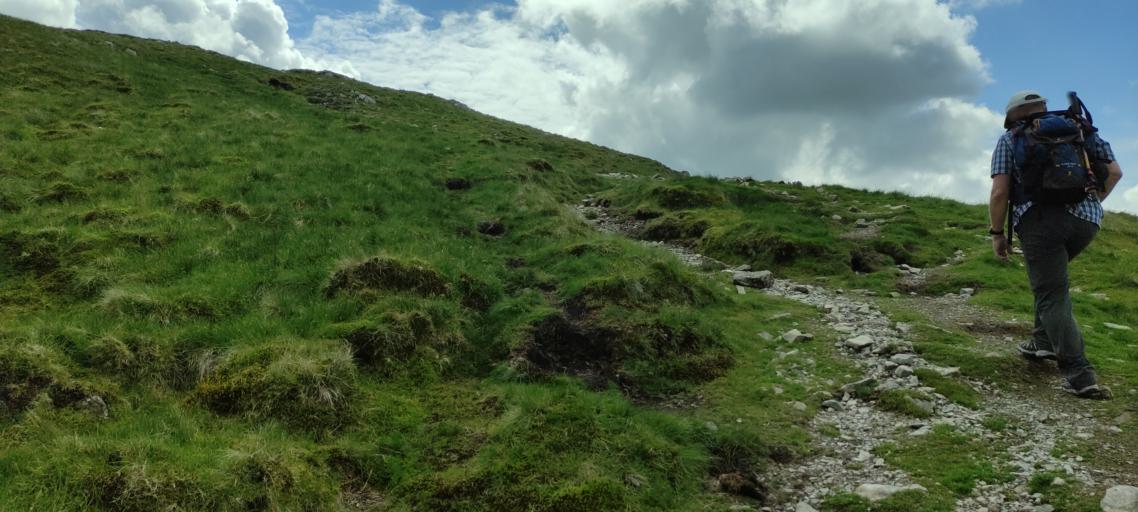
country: GB
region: England
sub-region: Cumbria
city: Windermere
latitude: 54.4697
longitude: -2.8746
